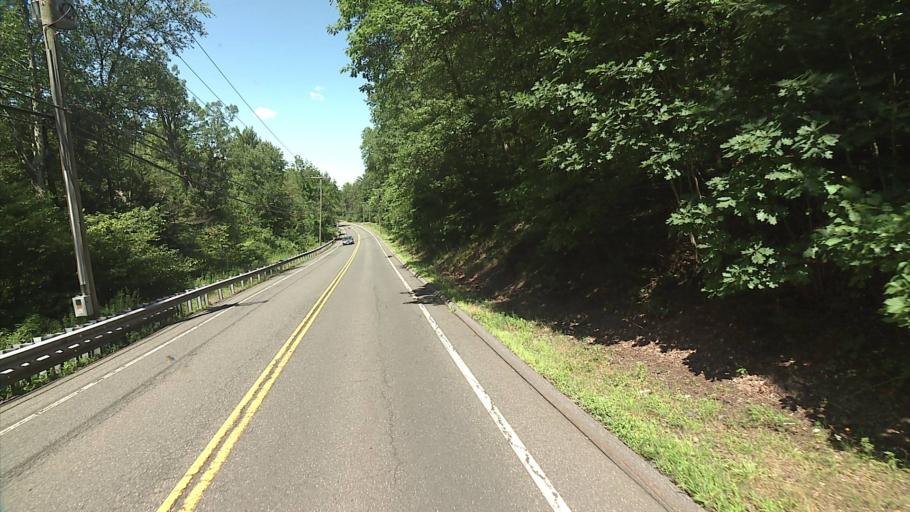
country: US
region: Massachusetts
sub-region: Hampden County
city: Southwick
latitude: 42.0075
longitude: -72.7256
